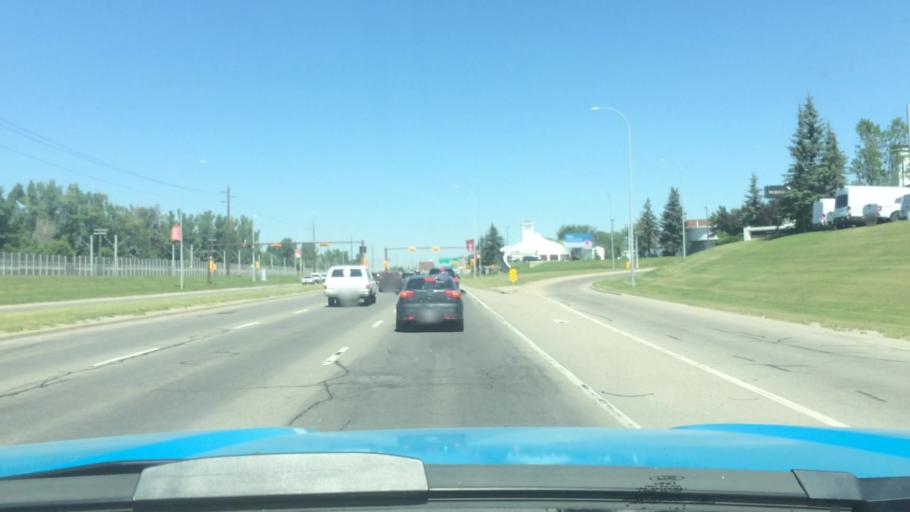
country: CA
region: Alberta
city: Calgary
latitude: 50.9382
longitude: -114.0690
